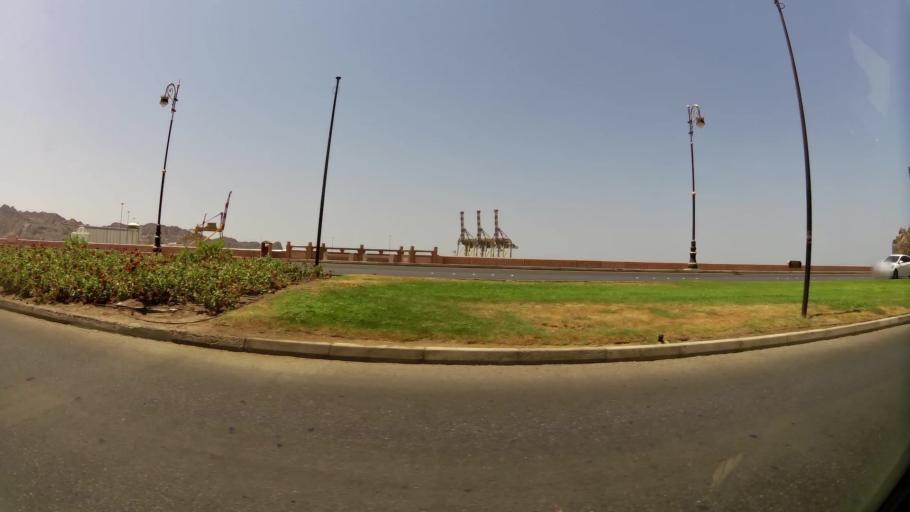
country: OM
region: Muhafazat Masqat
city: Muscat
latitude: 23.6225
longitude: 58.5714
